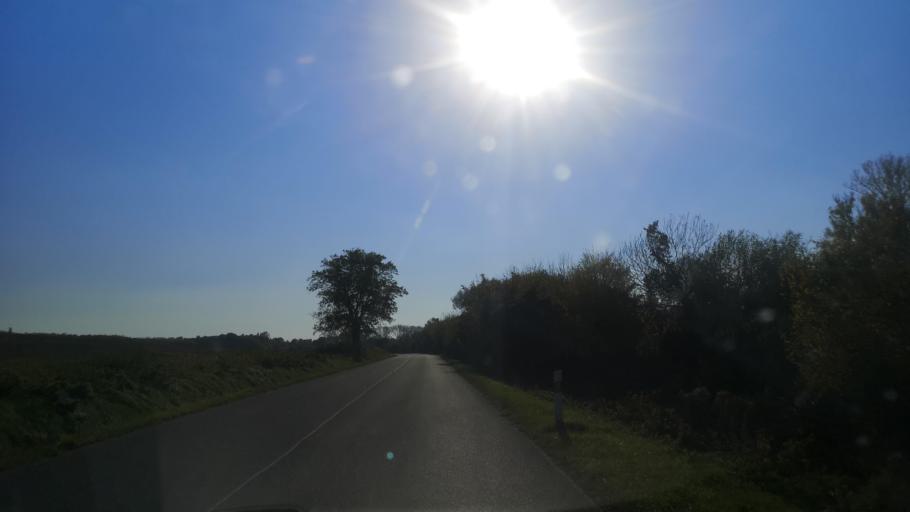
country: SK
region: Nitriansky
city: Zlate Moravce
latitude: 48.4399
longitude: 18.4312
